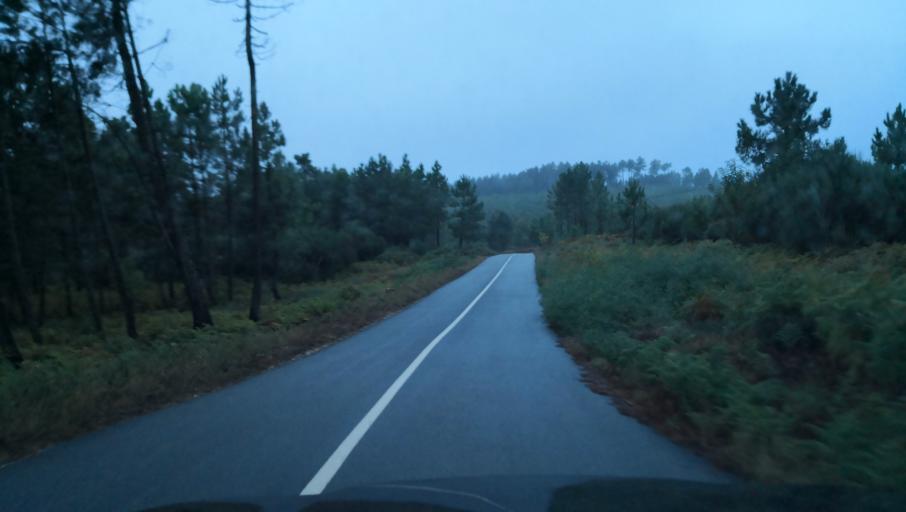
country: PT
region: Vila Real
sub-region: Sabrosa
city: Sabrosa
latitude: 41.2757
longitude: -7.5949
